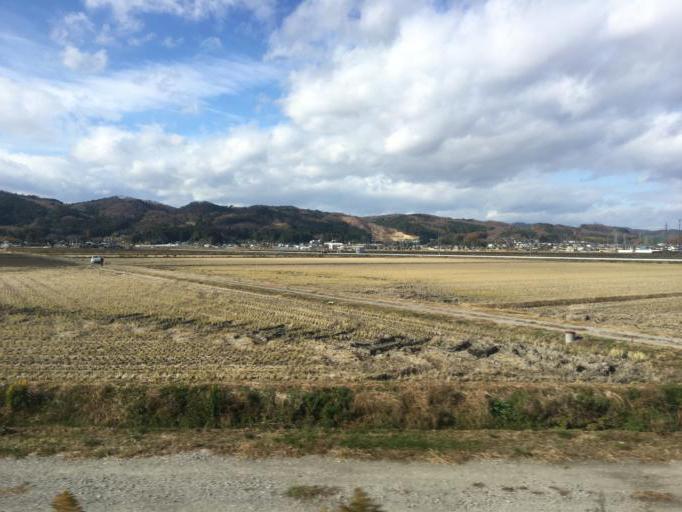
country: JP
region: Miyagi
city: Iwanuma
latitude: 38.1014
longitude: 140.8549
